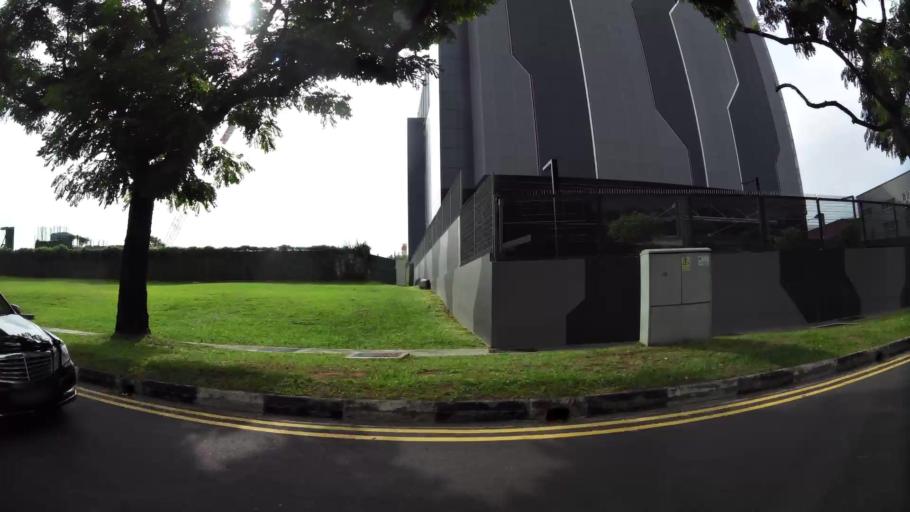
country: SG
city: Singapore
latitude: 1.3493
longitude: 103.8918
